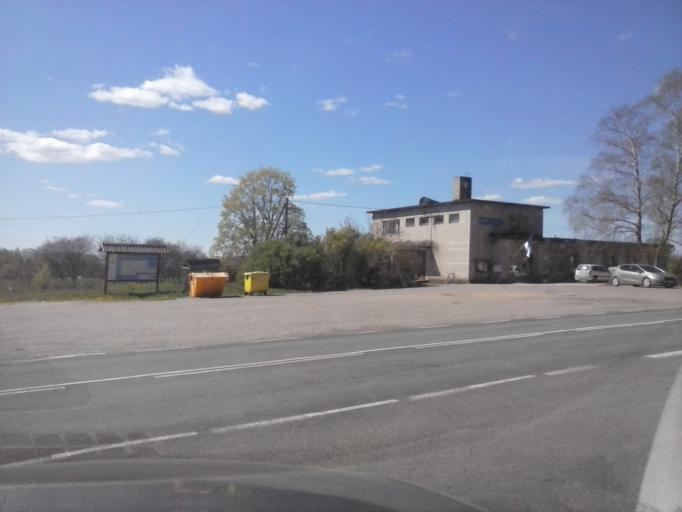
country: EE
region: Valgamaa
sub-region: Torva linn
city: Torva
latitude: 58.1490
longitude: 25.9736
